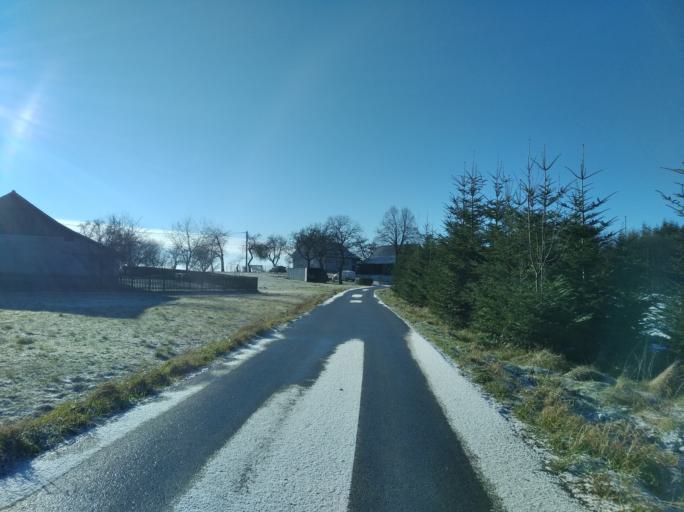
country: PL
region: Subcarpathian Voivodeship
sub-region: Powiat ropczycko-sedziszowski
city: Iwierzyce
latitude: 49.9695
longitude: 21.7500
